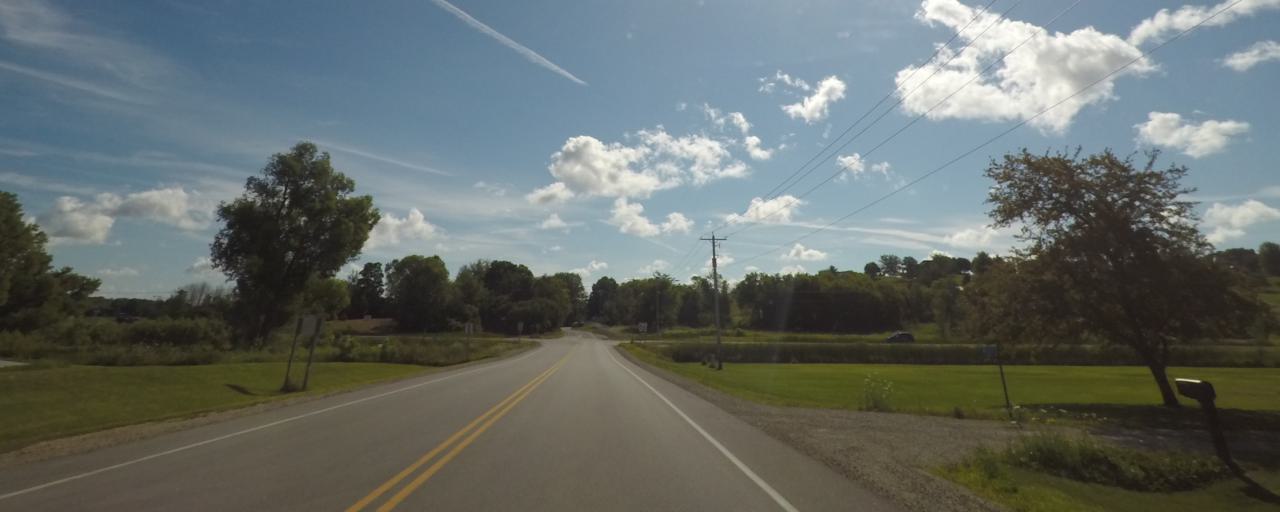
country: US
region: Wisconsin
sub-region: Jefferson County
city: Ixonia
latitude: 43.0690
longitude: -88.6021
